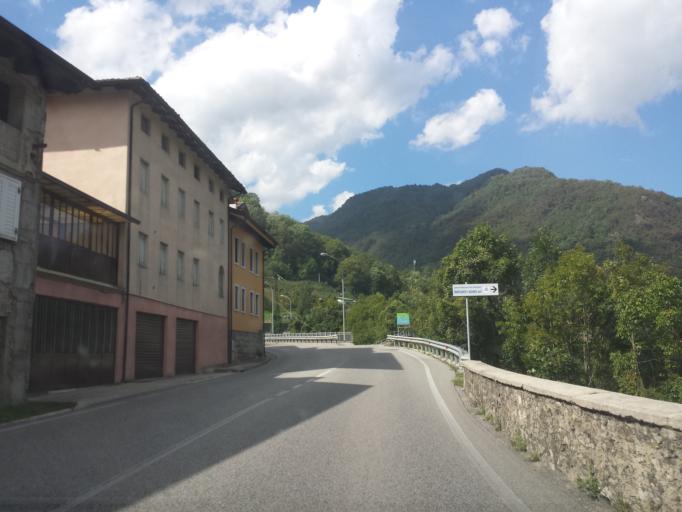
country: IT
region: Veneto
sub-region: Provincia di Vicenza
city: San Quirico
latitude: 45.6722
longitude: 11.2764
